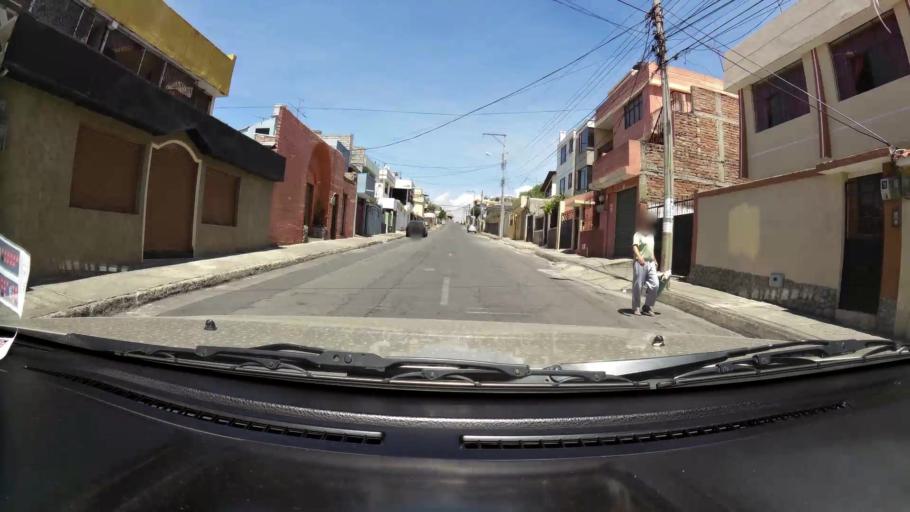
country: EC
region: Chimborazo
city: Riobamba
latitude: -1.6638
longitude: -78.6549
